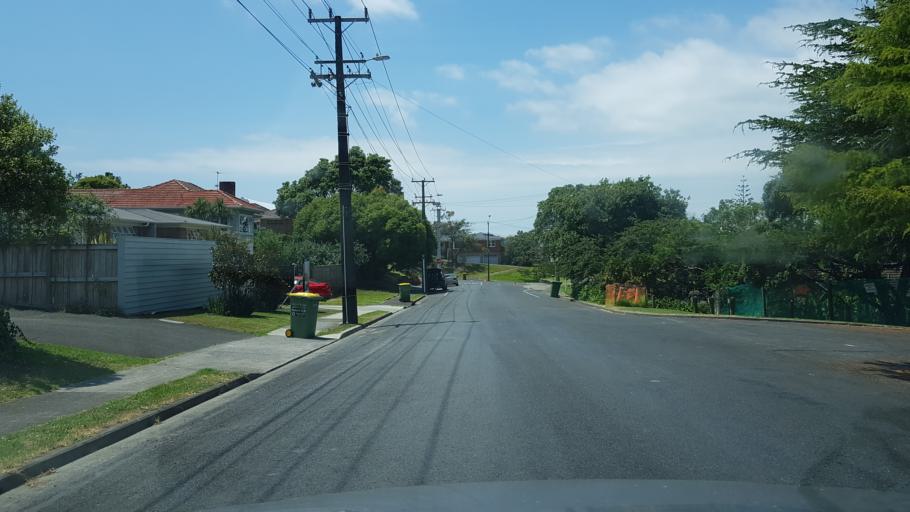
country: NZ
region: Auckland
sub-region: Auckland
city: North Shore
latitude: -36.8163
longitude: 174.7924
